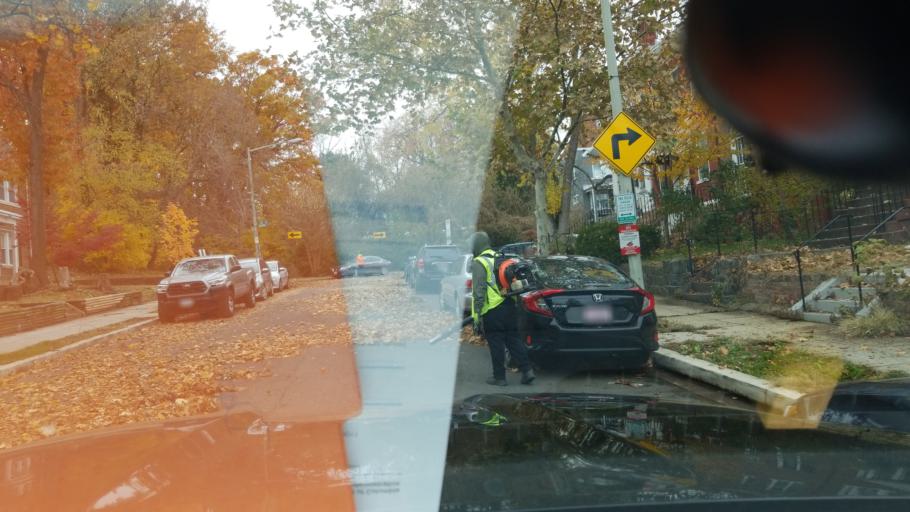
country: US
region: Washington, D.C.
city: Washington, D.C.
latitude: 38.9202
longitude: -77.0029
